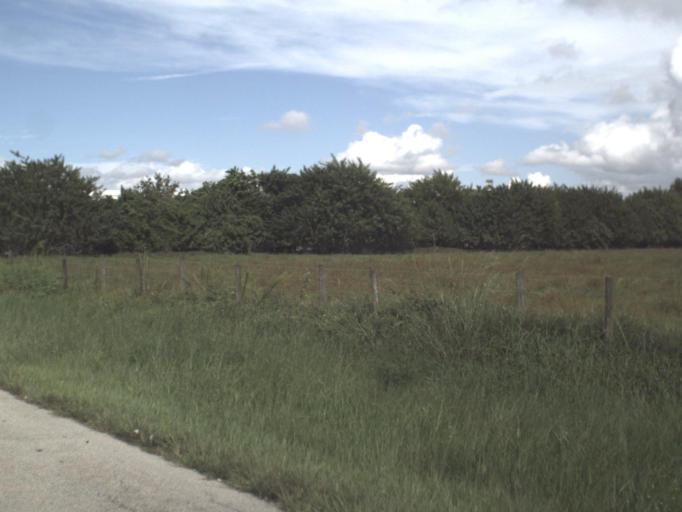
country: US
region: Florida
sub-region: Lee County
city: Fort Myers
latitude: 26.6204
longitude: -81.8520
